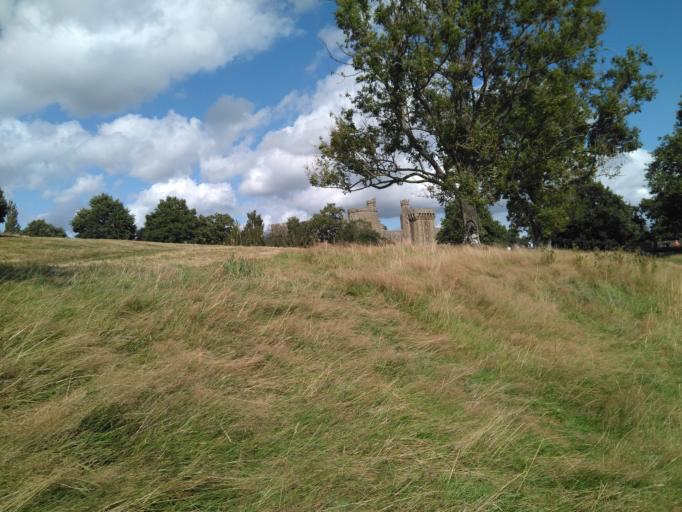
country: GB
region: England
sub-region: Kent
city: Hawkhurst
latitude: 51.0010
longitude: 0.5418
